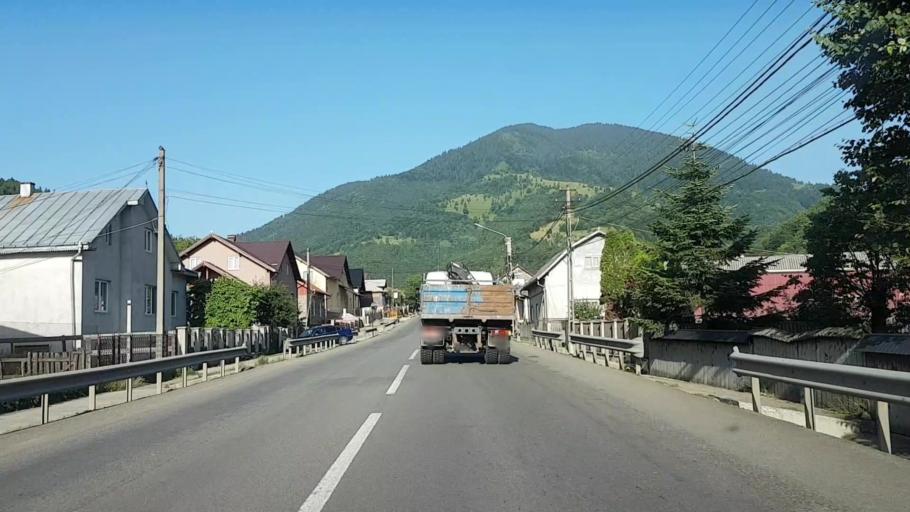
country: RO
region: Bistrita-Nasaud
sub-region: Comuna Tiha Bargaului
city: Tureac
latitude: 47.2101
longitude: 24.8602
